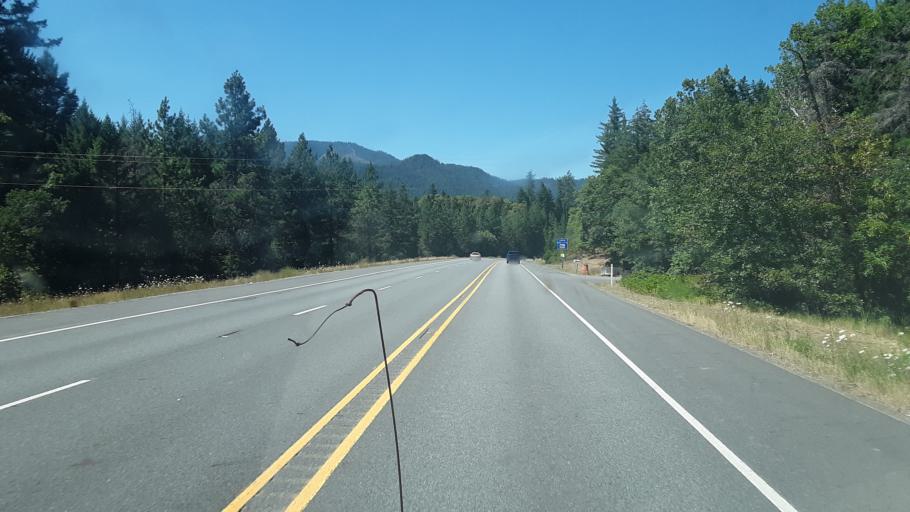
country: US
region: Oregon
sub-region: Josephine County
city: Cave Junction
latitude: 42.2657
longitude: -123.6190
